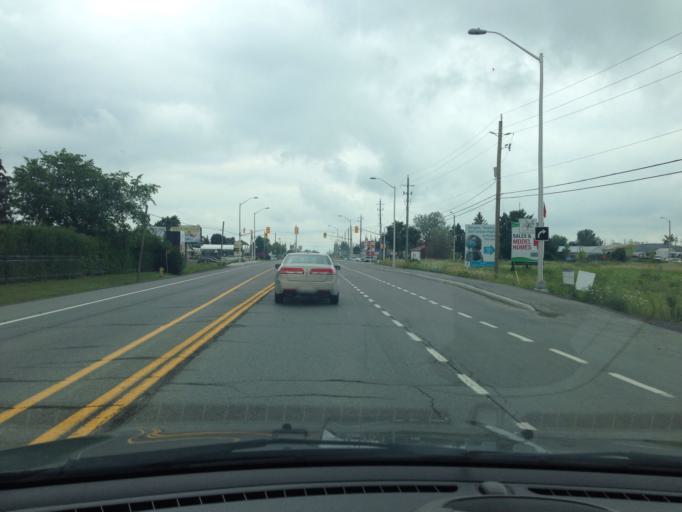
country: CA
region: Ontario
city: Ottawa
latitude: 45.3263
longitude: -75.5971
